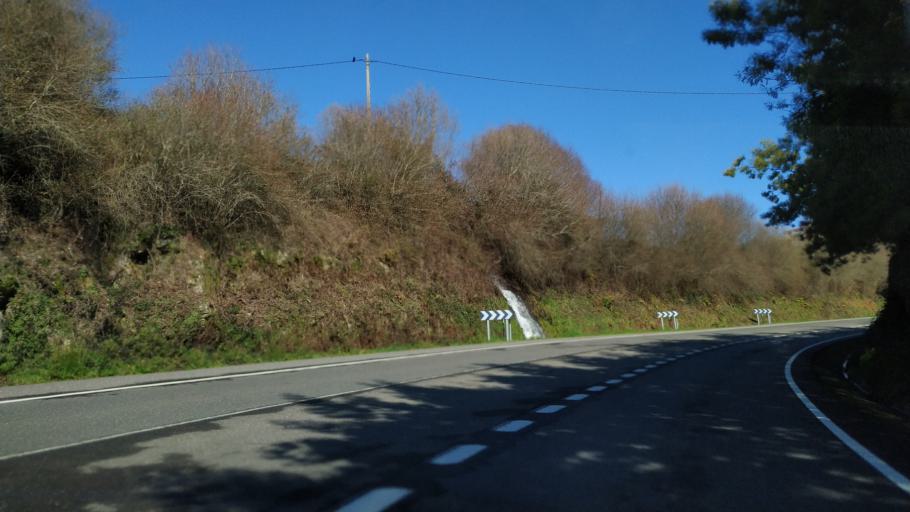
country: ES
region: Galicia
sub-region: Provincia de Ourense
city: Pinor
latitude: 42.5185
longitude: -8.0144
